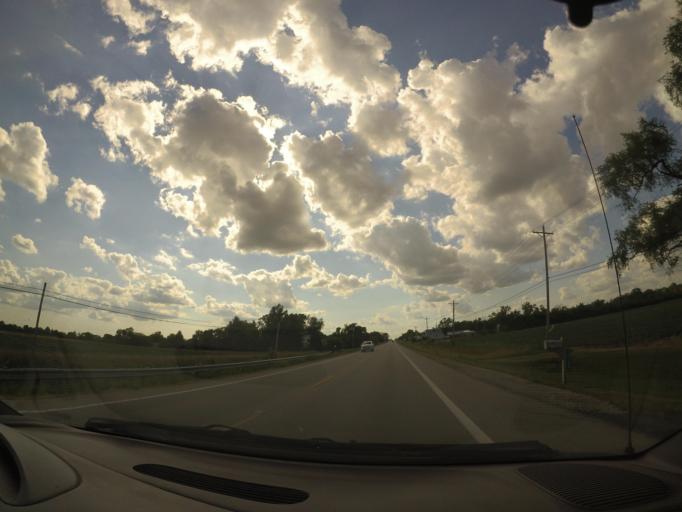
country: US
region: Ohio
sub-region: Wood County
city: Luckey
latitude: 41.5049
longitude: -83.4958
